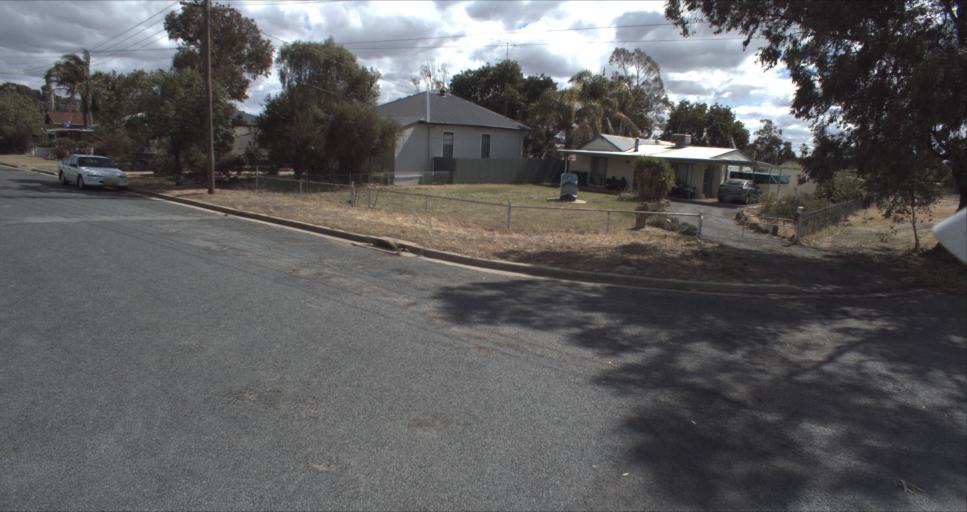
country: AU
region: New South Wales
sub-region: Leeton
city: Leeton
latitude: -34.6005
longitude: 146.4093
